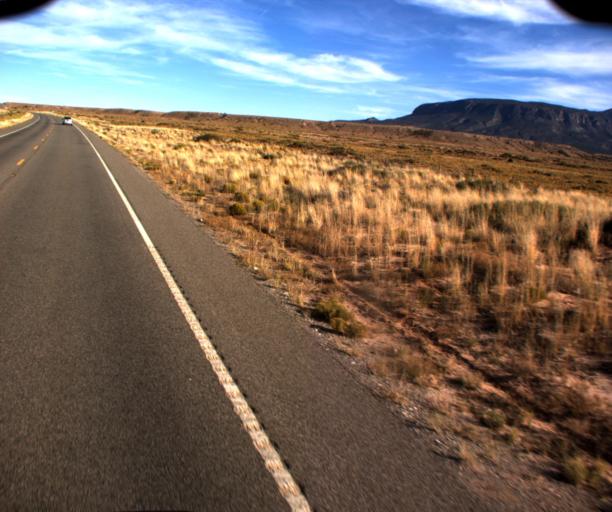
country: US
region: Arizona
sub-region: Apache County
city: Lukachukai
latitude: 36.9303
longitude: -109.2179
